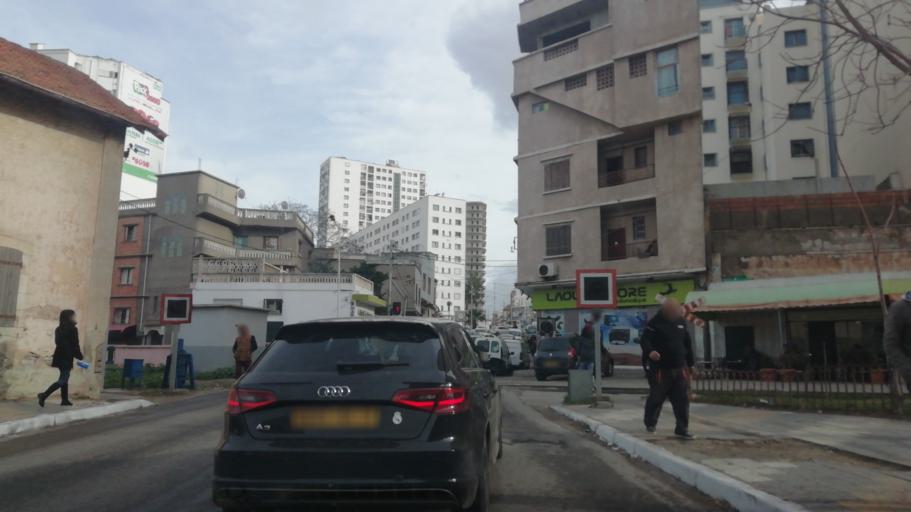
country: DZ
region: Oran
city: Oran
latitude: 35.7018
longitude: -0.6312
